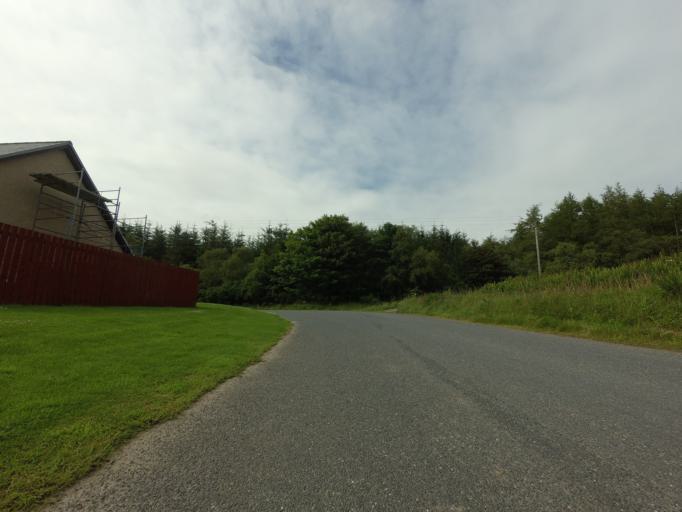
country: GB
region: Scotland
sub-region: Aberdeenshire
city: Turriff
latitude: 57.5358
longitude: -2.4031
